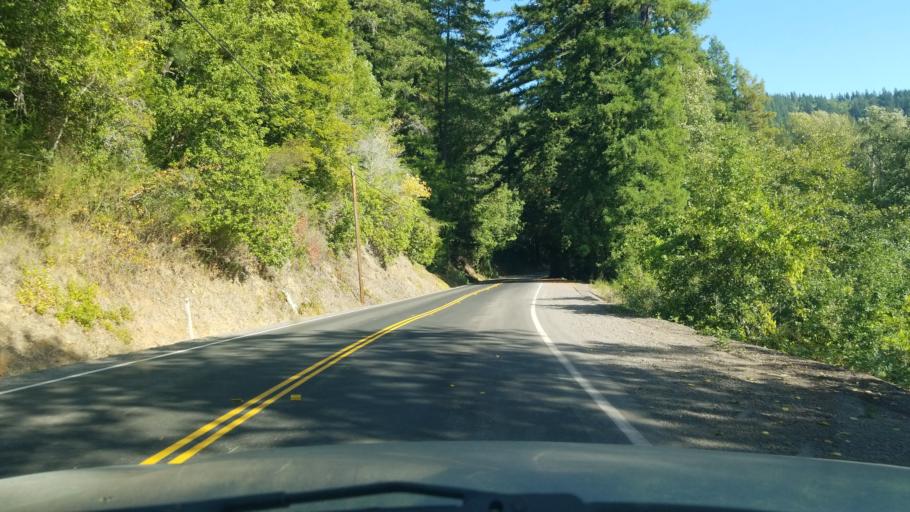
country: US
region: California
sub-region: Humboldt County
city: Redway
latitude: 40.2223
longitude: -123.7891
